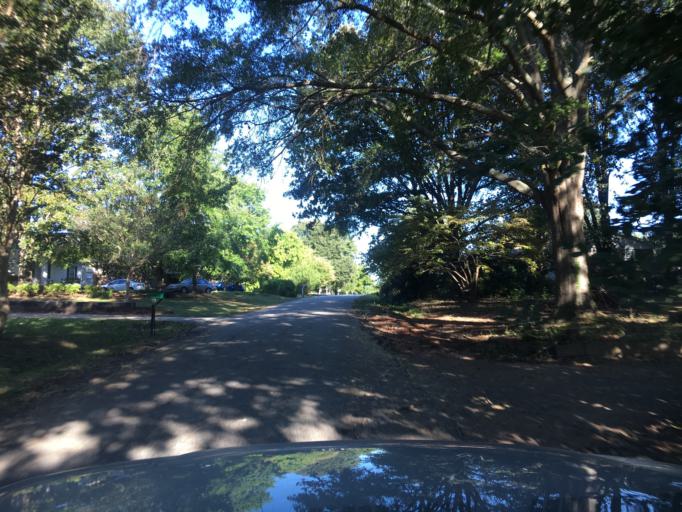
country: US
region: South Carolina
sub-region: Spartanburg County
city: Lyman
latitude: 34.9213
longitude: -82.1196
